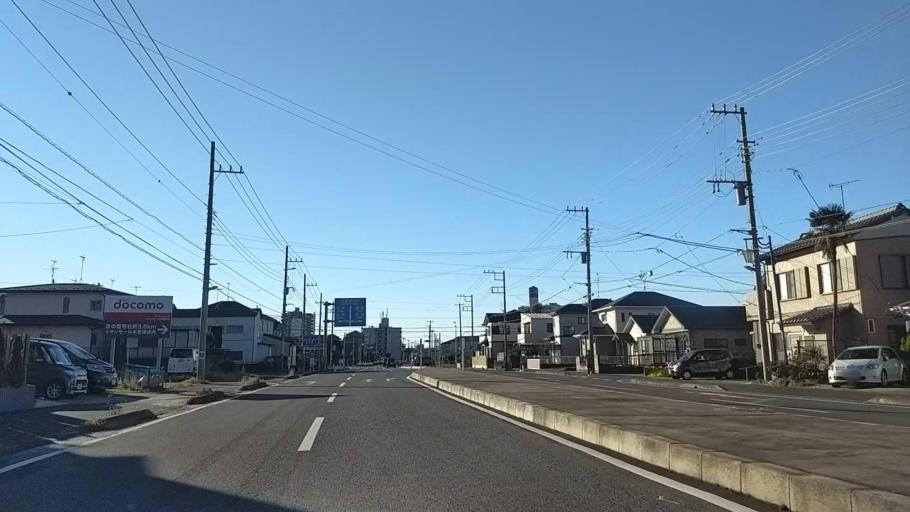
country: JP
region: Chiba
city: Kisarazu
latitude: 35.3876
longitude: 139.9203
